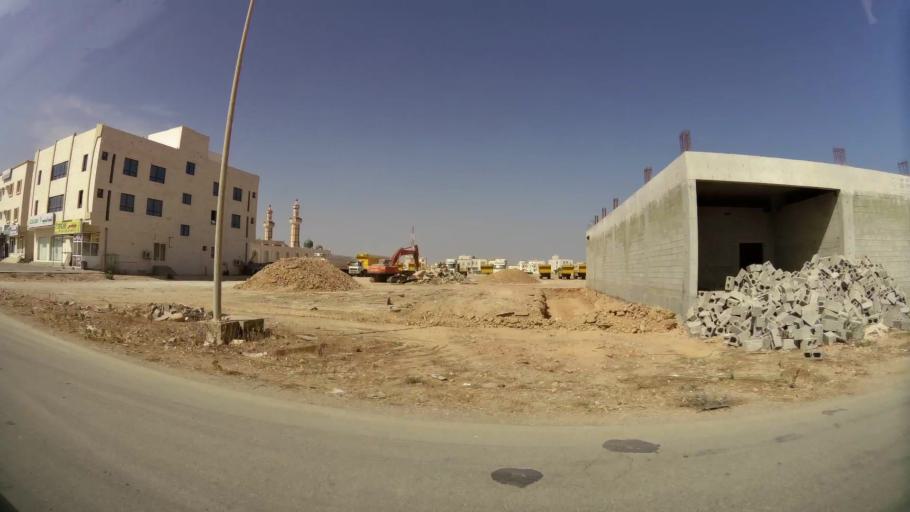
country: OM
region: Zufar
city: Salalah
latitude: 16.9994
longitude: 54.0114
